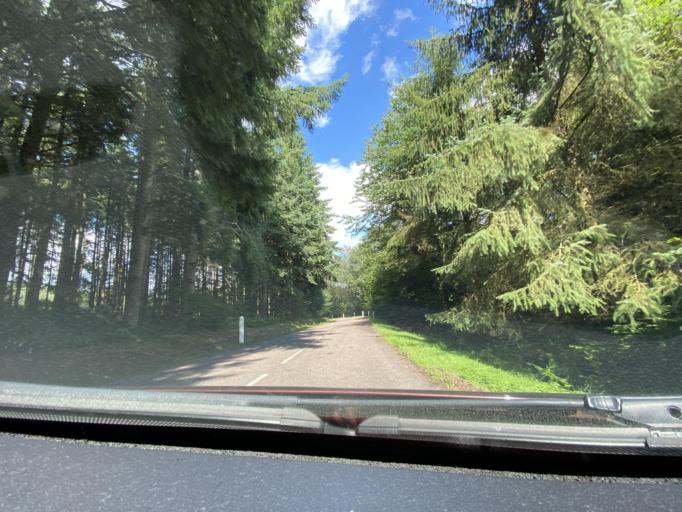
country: FR
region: Bourgogne
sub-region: Departement de la Cote-d'Or
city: Saulieu
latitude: 47.2696
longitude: 4.1242
